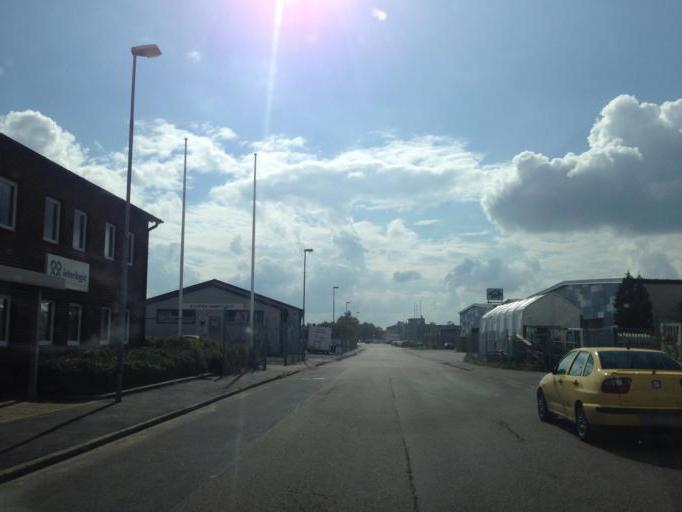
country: SE
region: Skane
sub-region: Lomma Kommun
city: Lomma
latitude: 55.6810
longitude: 13.0803
